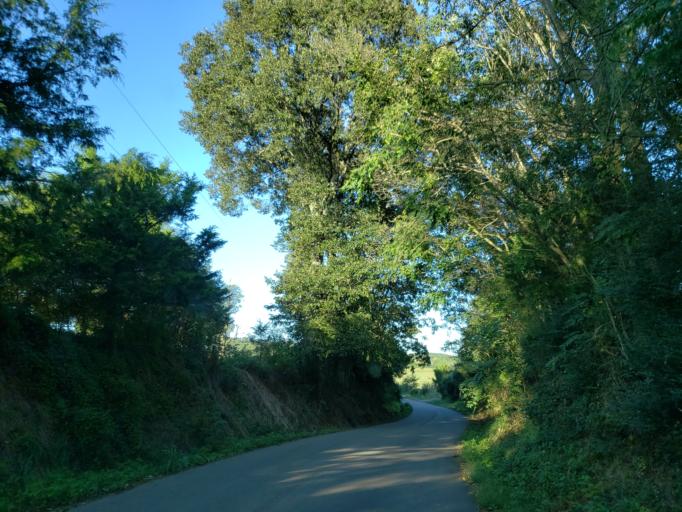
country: US
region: Georgia
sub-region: Bartow County
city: Rydal
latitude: 34.3279
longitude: -84.7271
